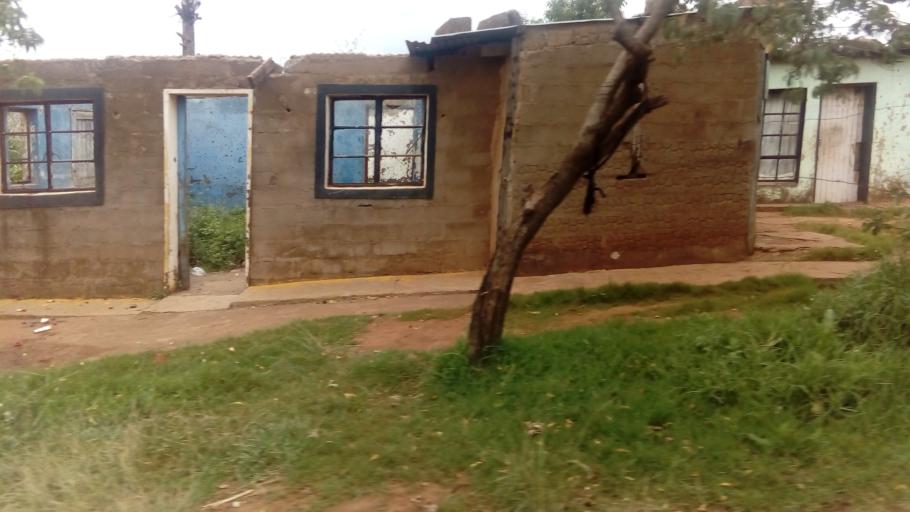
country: LS
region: Leribe
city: Leribe
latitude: -29.0074
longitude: 28.2133
